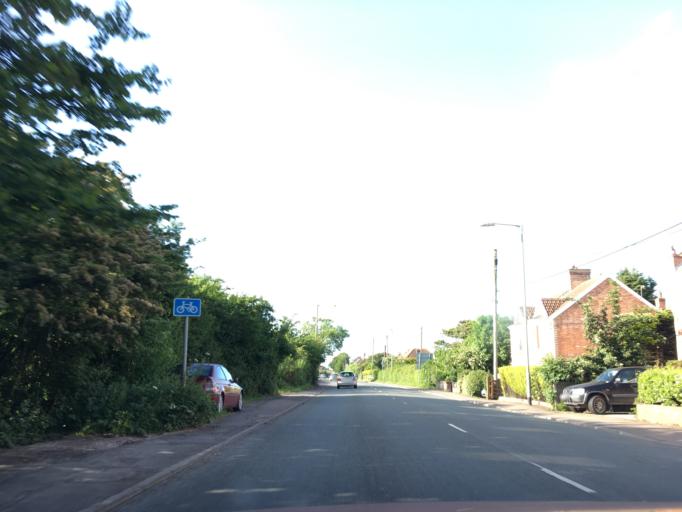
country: GB
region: England
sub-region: Somerset
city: Highbridge
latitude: 51.2102
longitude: -2.9854
